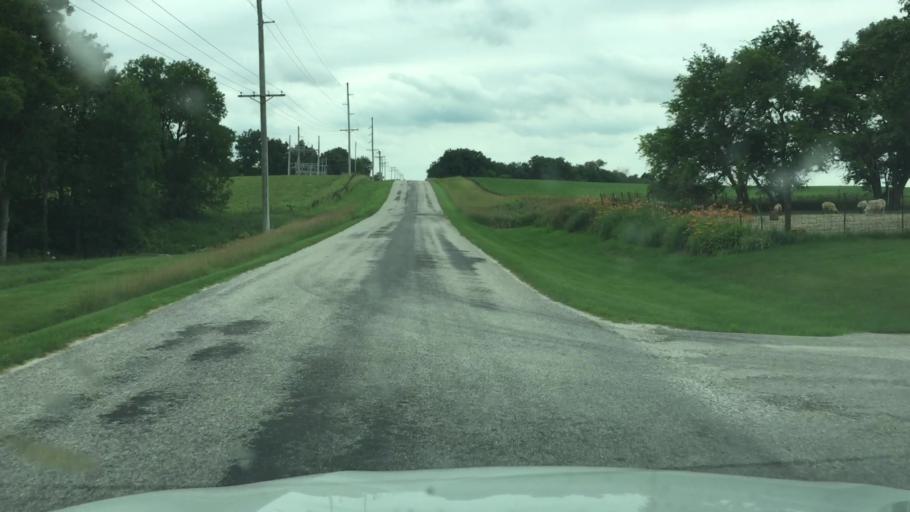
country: US
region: Illinois
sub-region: Hancock County
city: Carthage
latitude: 40.2980
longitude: -91.0832
